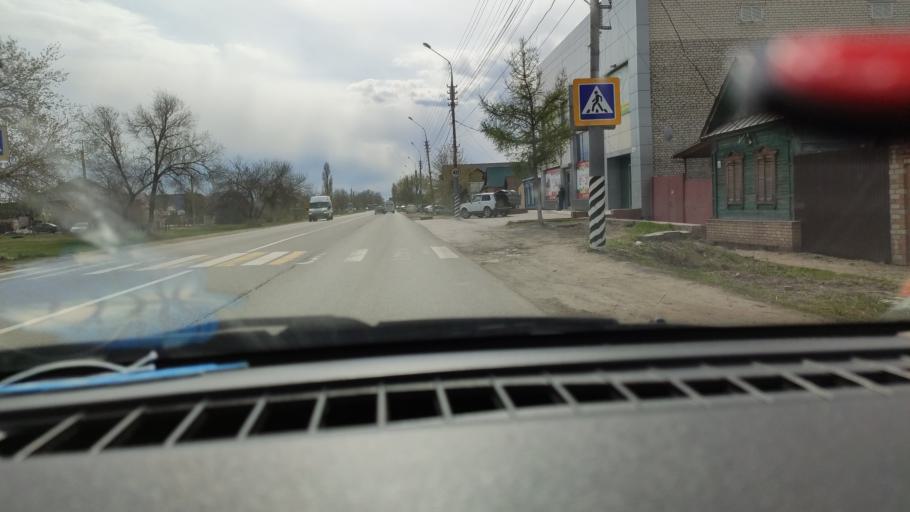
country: RU
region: Saratov
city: Privolzhskiy
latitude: 51.4263
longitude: 46.0480
